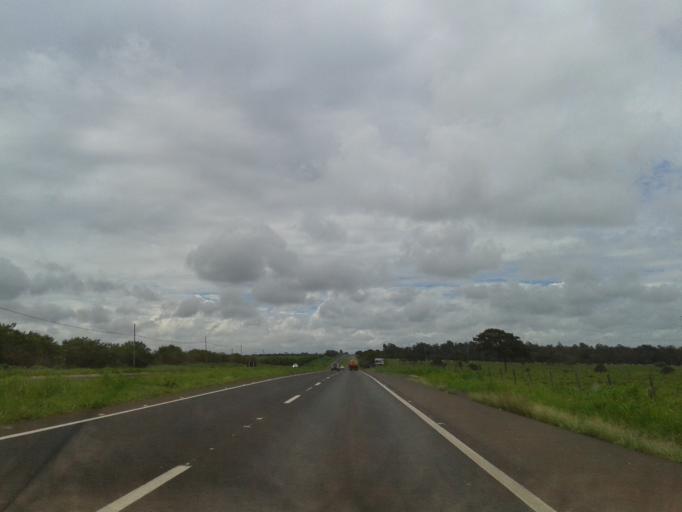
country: BR
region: Minas Gerais
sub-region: Uberlandia
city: Uberlandia
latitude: -18.8793
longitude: -48.5022
